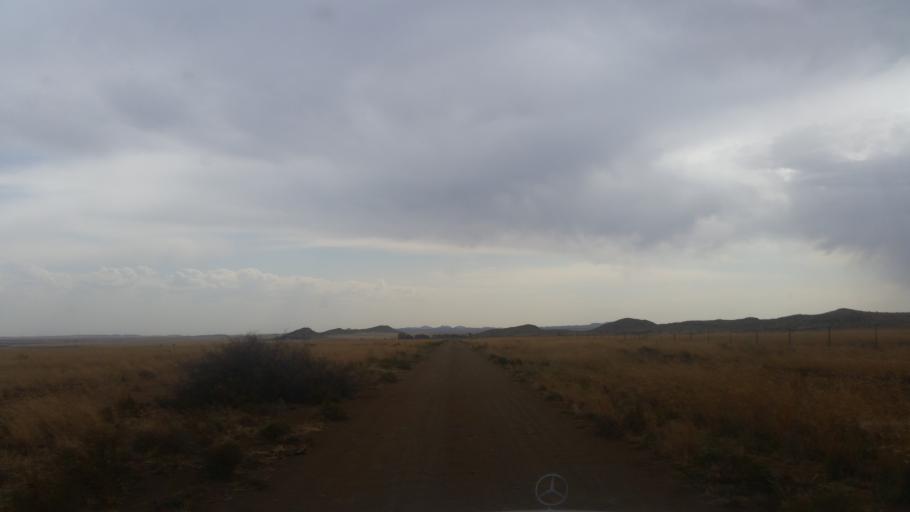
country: ZA
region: Orange Free State
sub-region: Xhariep District Municipality
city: Trompsburg
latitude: -30.5069
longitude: 25.9249
